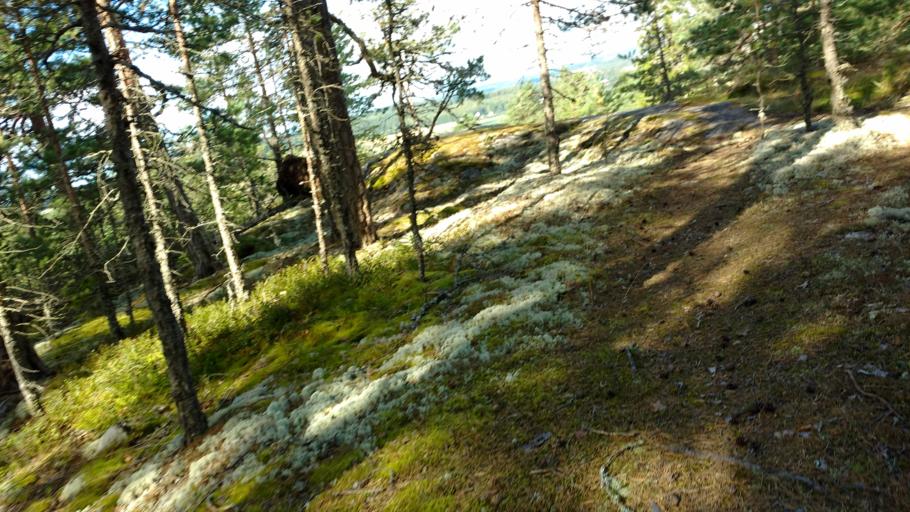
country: FI
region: Varsinais-Suomi
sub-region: Salo
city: Salo
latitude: 60.3723
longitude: 23.1762
